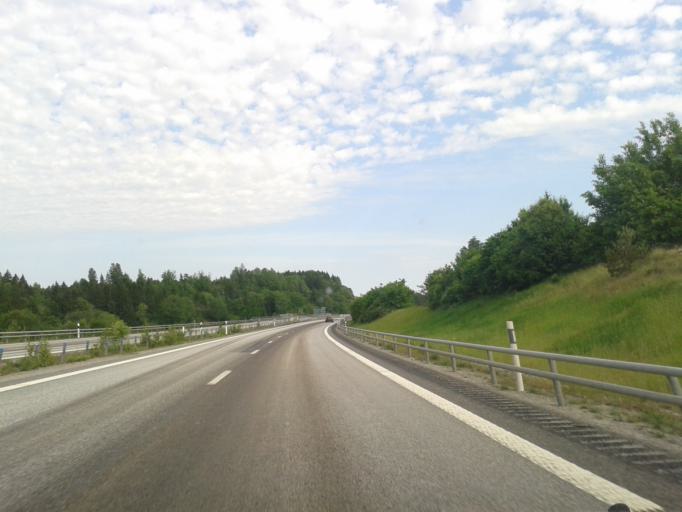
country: SE
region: Vaestra Goetaland
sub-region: Munkedals Kommun
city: Munkedal
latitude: 58.4923
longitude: 11.5760
